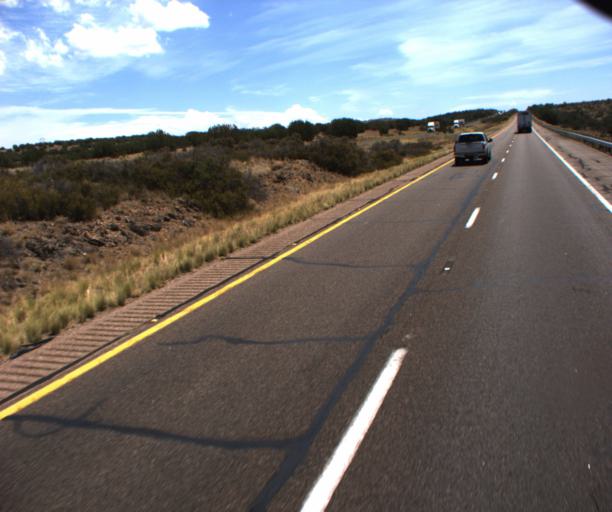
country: US
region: Arizona
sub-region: Yavapai County
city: Paulden
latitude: 35.2835
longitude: -112.7964
